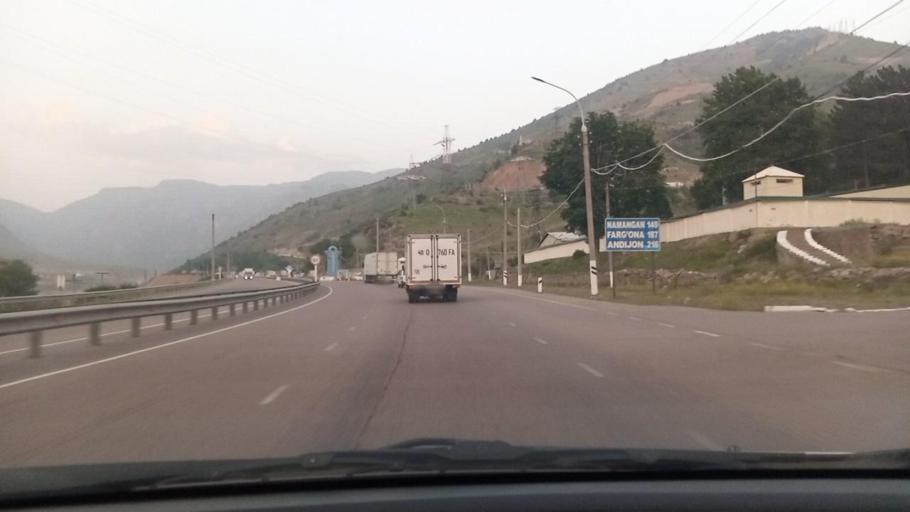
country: UZ
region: Toshkent
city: Angren
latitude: 41.1523
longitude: 70.4391
